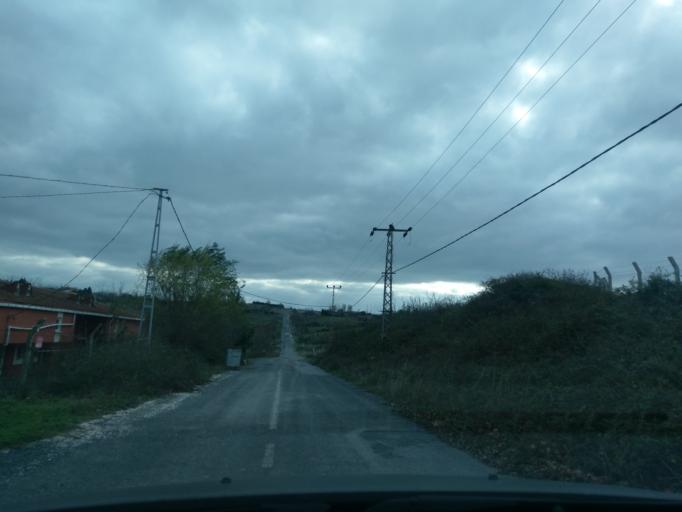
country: TR
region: Istanbul
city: Durusu
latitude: 41.2903
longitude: 28.6862
